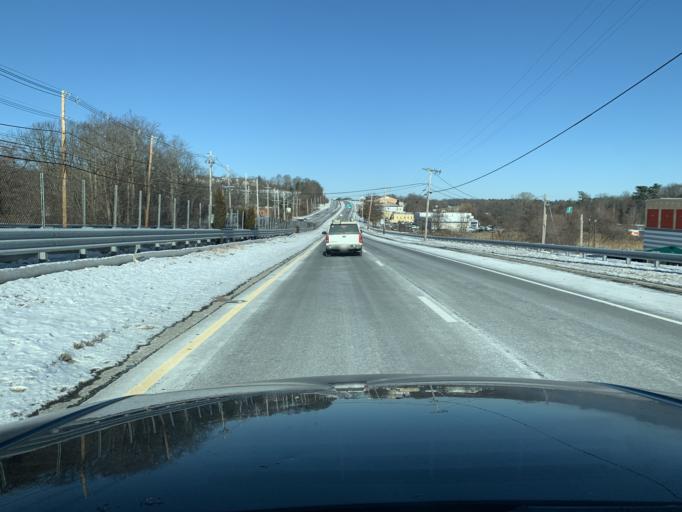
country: US
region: Massachusetts
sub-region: Essex County
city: Danvers
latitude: 42.5714
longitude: -70.9727
